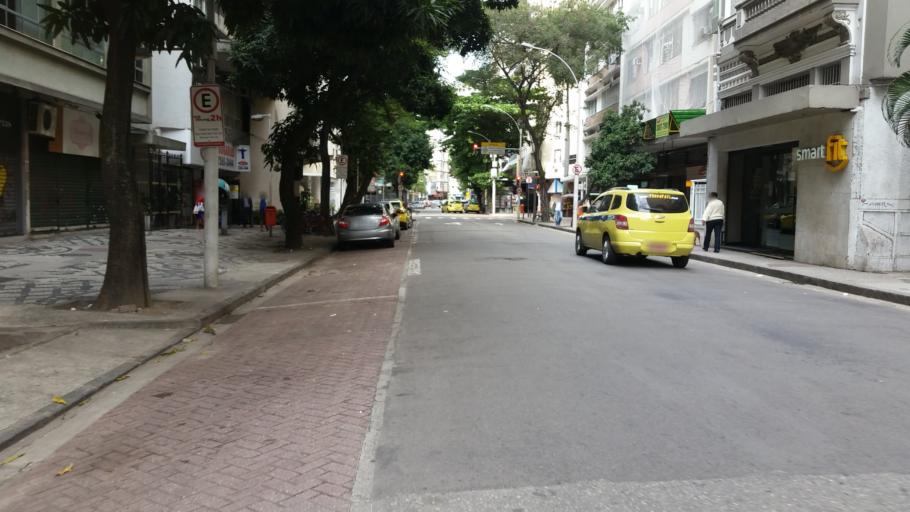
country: BR
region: Rio de Janeiro
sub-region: Rio De Janeiro
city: Rio de Janeiro
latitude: -22.9337
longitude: -43.1773
